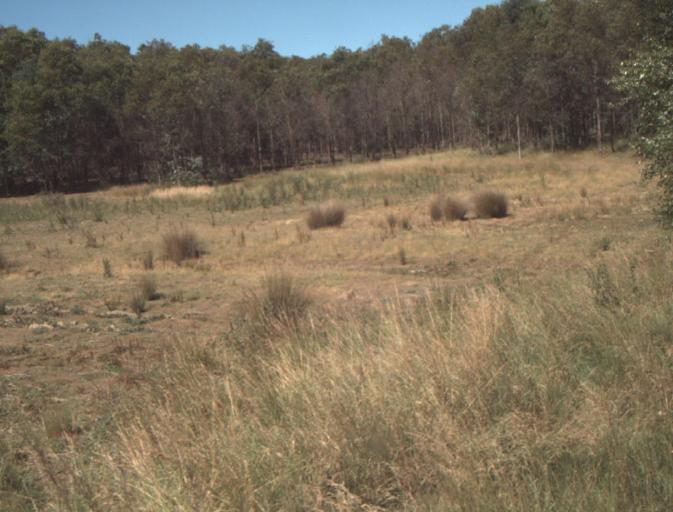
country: AU
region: Tasmania
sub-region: Dorset
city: Scottsdale
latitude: -41.2704
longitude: 147.3514
